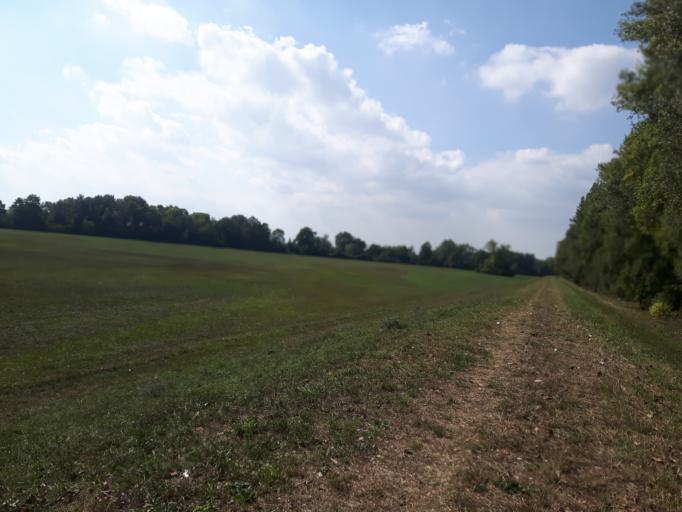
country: DE
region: Rheinland-Pfalz
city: Altrip
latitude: 49.3981
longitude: 8.4909
